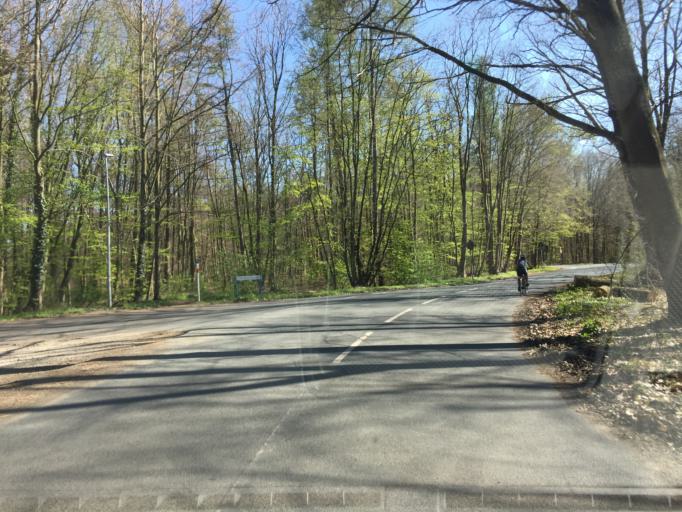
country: DE
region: Lower Saxony
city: Gross Munzel
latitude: 52.4139
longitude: 9.5060
